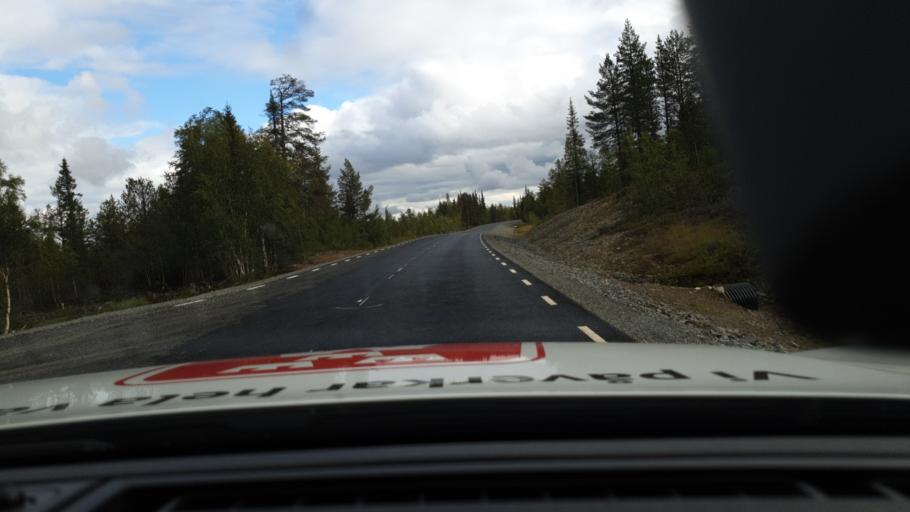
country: SE
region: Norrbotten
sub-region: Gallivare Kommun
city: Gaellivare
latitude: 66.8540
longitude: 21.1071
